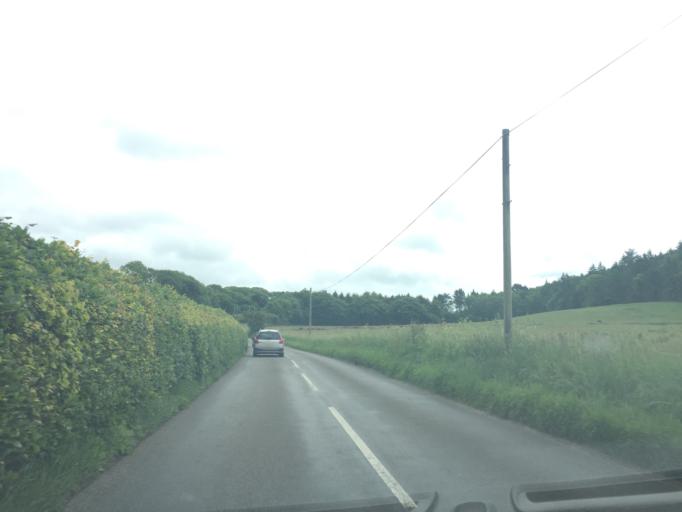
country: GB
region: England
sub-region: Dorset
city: Swanage
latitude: 50.6393
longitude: -2.0138
